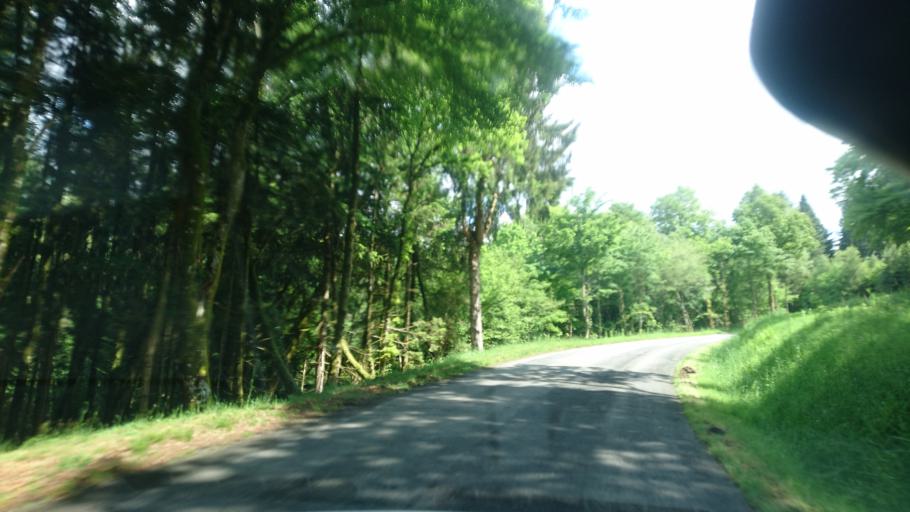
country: FR
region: Limousin
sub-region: Departement de la Haute-Vienne
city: Peyrat-le-Chateau
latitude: 45.7760
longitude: 1.8722
